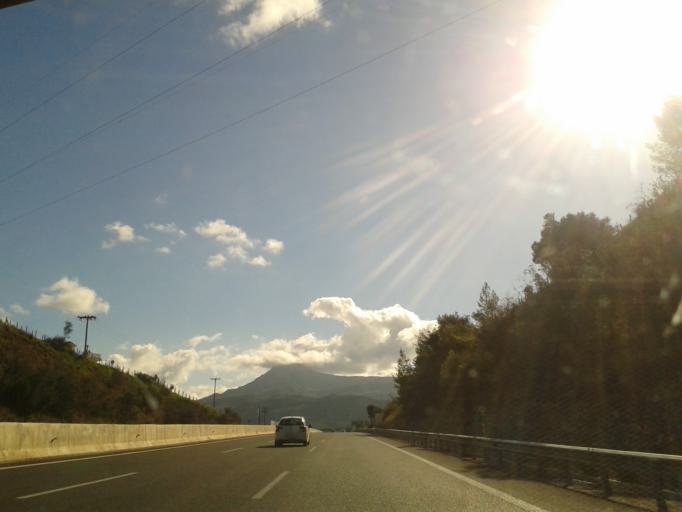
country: GR
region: West Greece
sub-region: Nomos Achaias
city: Aigio
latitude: 38.2488
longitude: 22.0713
